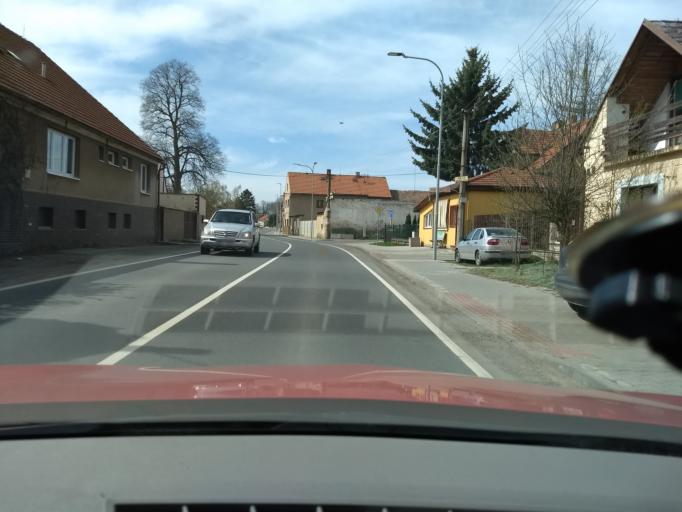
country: CZ
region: Central Bohemia
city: Jenec
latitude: 50.0511
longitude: 14.1784
